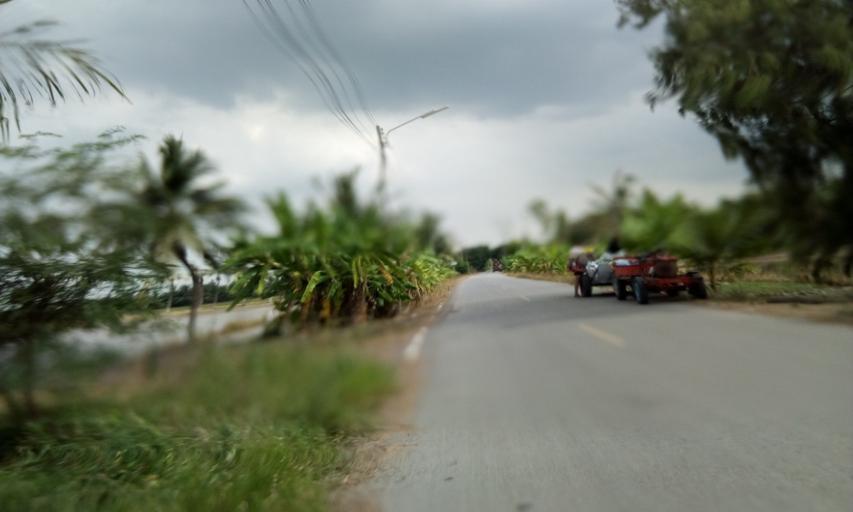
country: TH
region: Pathum Thani
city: Ban Lam Luk Ka
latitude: 14.0235
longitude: 100.8470
